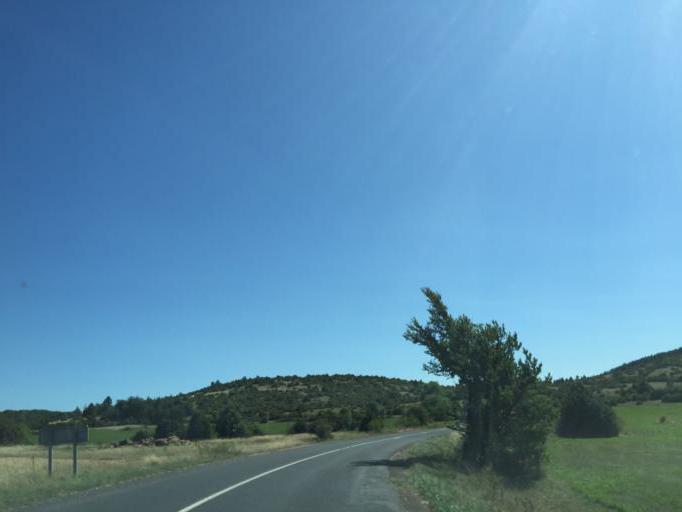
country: FR
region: Languedoc-Roussillon
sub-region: Departement de l'Herault
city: Lodeve
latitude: 43.8997
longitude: 3.3110
